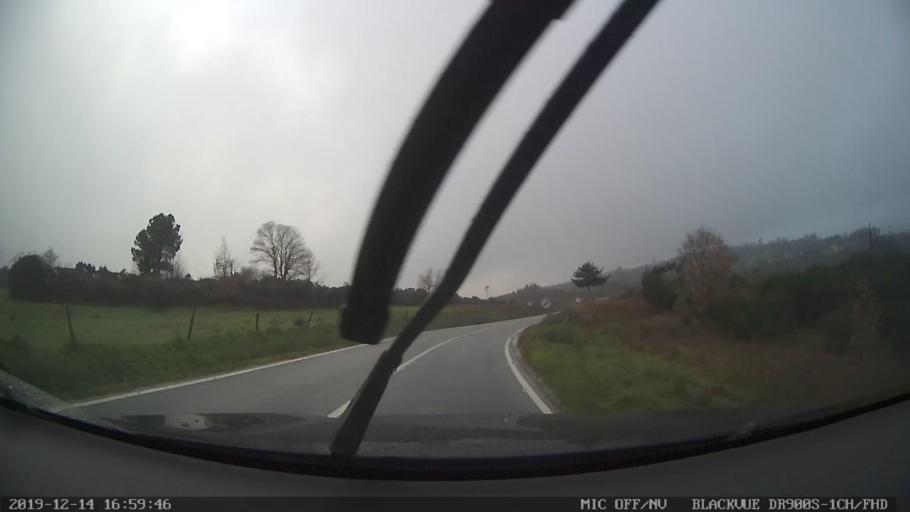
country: PT
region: Vila Real
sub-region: Vila Pouca de Aguiar
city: Vila Pouca de Aguiar
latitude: 41.4371
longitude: -7.5660
